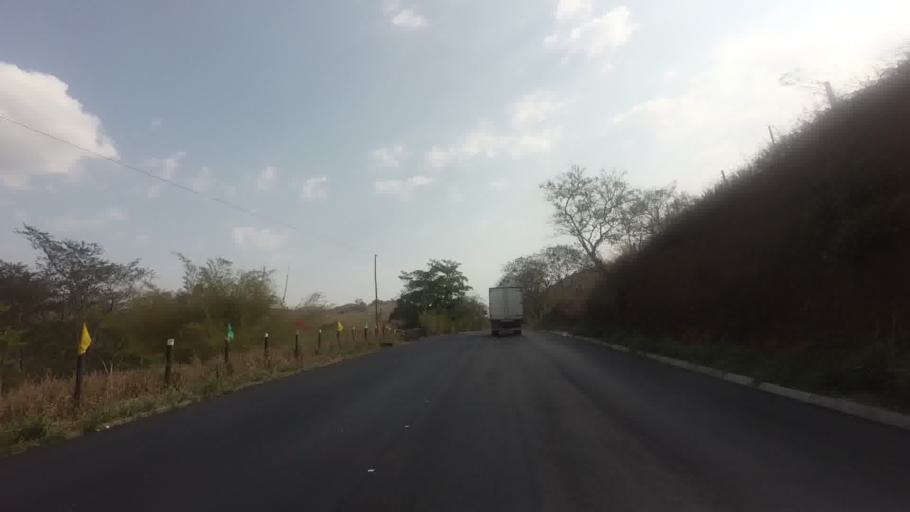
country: BR
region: Rio de Janeiro
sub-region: Bom Jesus Do Itabapoana
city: Bom Jesus do Itabapoana
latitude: -21.1632
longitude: -41.6759
